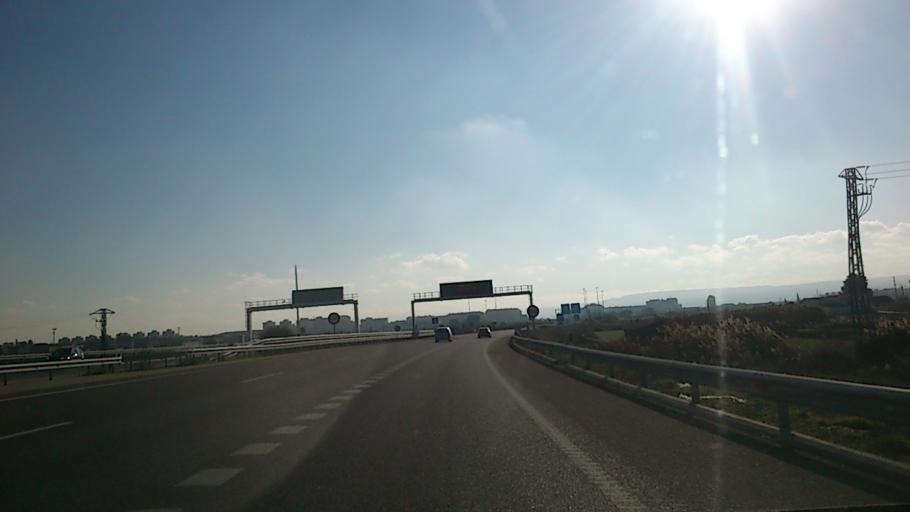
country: ES
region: Aragon
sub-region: Provincia de Zaragoza
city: Zaragoza
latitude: 41.6864
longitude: -0.8328
